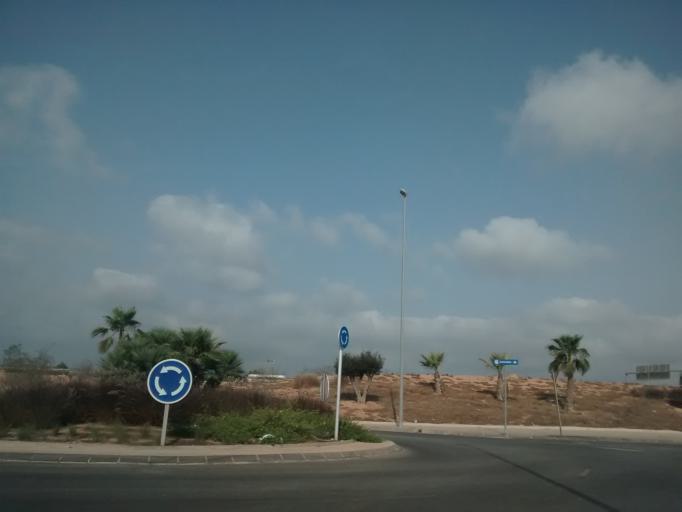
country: ES
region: Valencia
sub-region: Provincia de Alicante
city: San Miguel de Salinas
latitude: 37.9287
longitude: -0.7378
